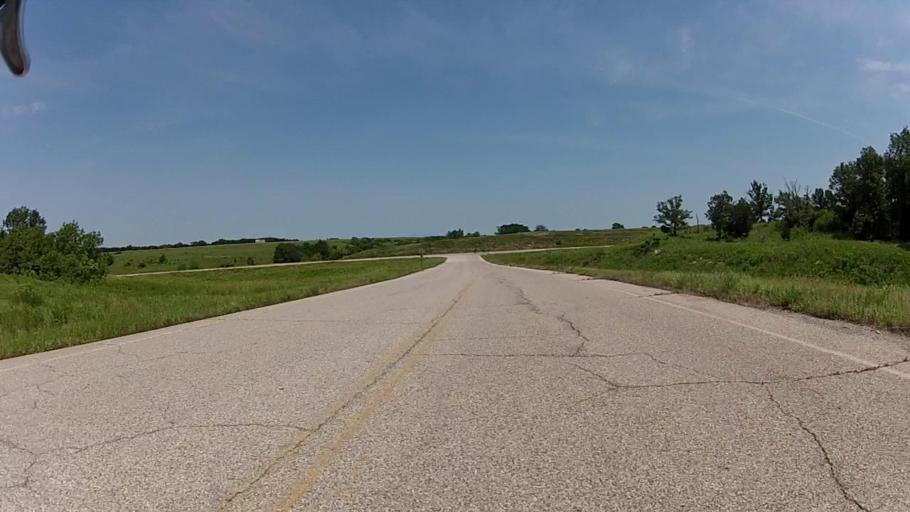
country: US
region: Kansas
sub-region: Chautauqua County
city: Sedan
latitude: 37.1129
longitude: -96.4734
